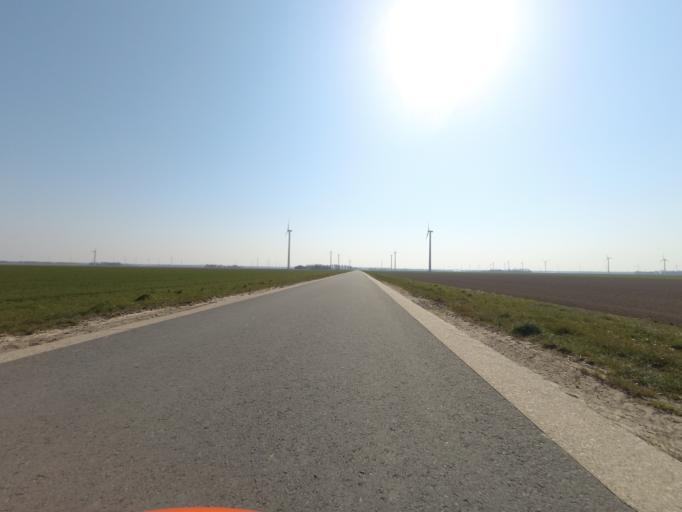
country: NL
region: Utrecht
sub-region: Gemeente Bunschoten
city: Spakenburg
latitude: 52.3425
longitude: 5.3770
